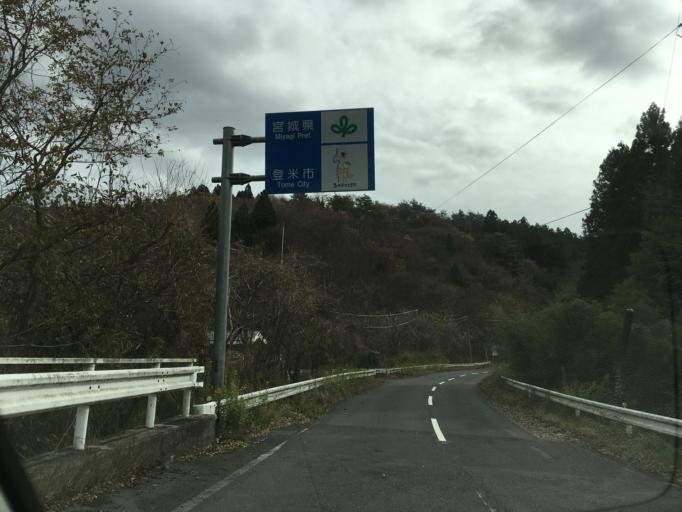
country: JP
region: Iwate
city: Ichinoseki
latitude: 38.7882
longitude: 141.2642
